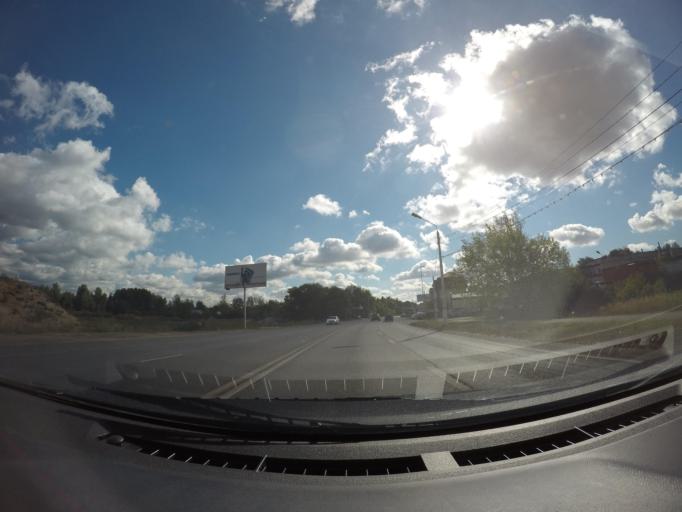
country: RU
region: Moskovskaya
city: Ramenskoye
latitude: 55.5857
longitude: 38.2354
